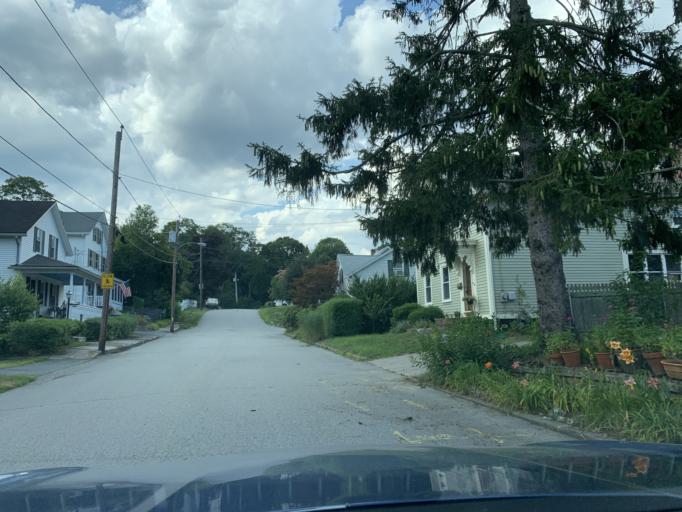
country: US
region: Rhode Island
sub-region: Kent County
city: East Greenwich
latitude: 41.6658
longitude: -71.4474
